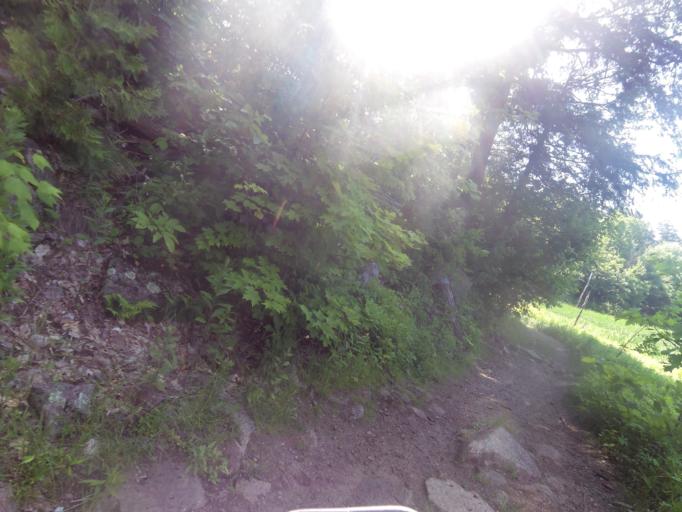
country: CA
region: Quebec
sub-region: Outaouais
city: Wakefield
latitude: 45.5392
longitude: -75.8772
